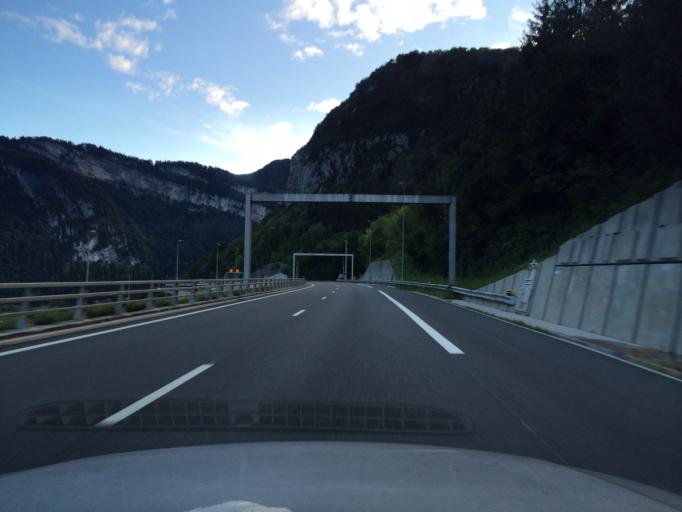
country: FR
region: Rhone-Alpes
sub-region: Departement de l'Ain
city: Nantua
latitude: 46.1477
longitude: 5.6359
